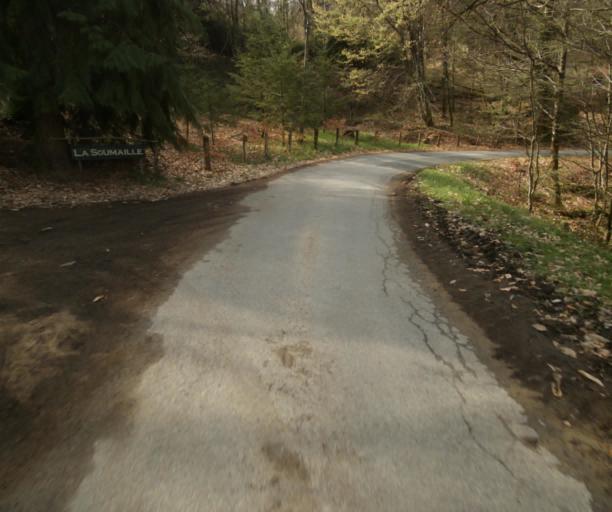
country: FR
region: Limousin
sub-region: Departement de la Correze
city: Correze
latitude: 45.3420
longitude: 1.8457
